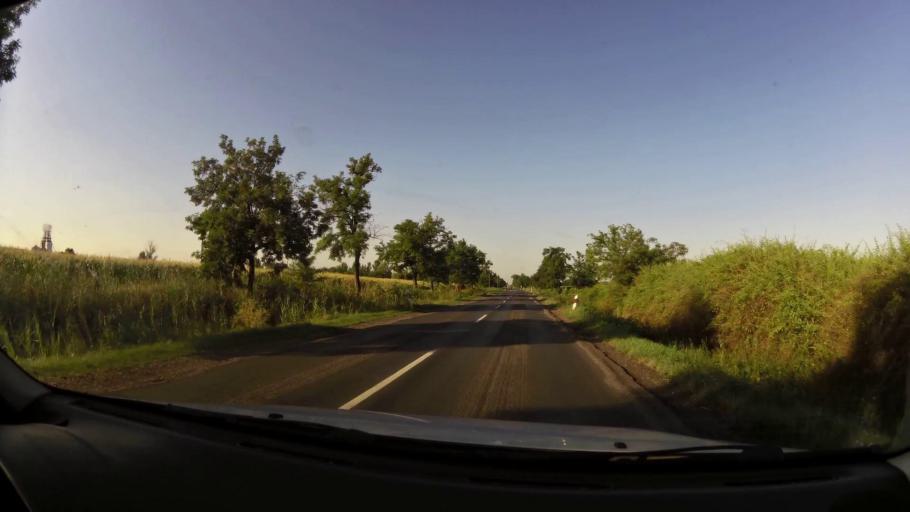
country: HU
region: Pest
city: Cegled
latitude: 47.2302
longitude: 19.8351
